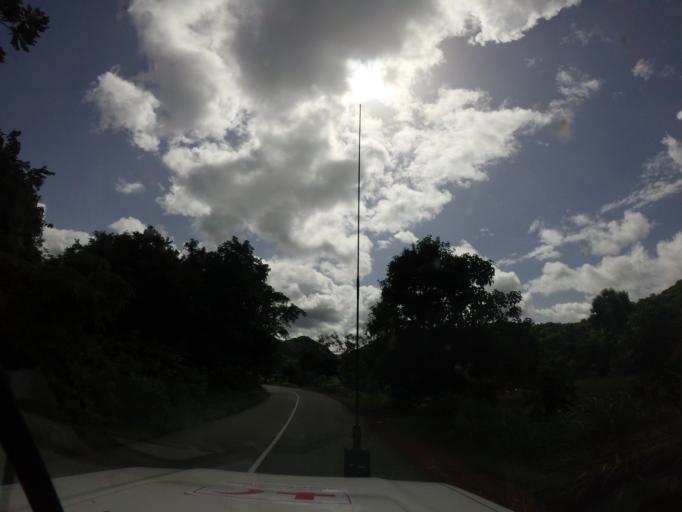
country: GN
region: Mamou
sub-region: Mamou Prefecture
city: Mamou
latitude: 10.2810
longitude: -11.9233
